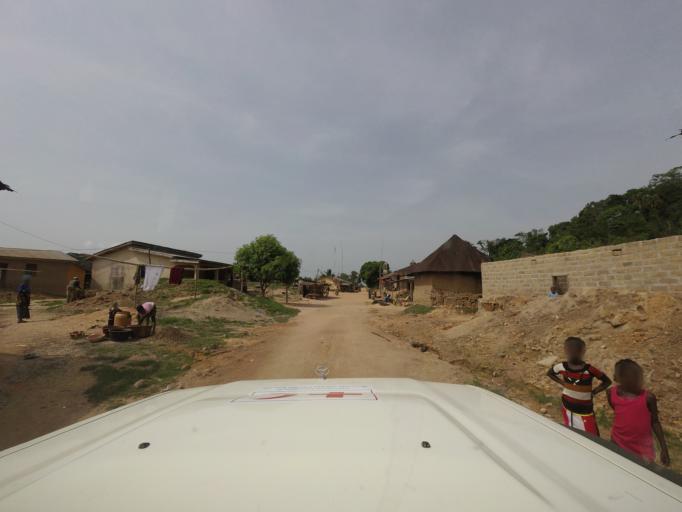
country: GN
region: Nzerekore
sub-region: Macenta
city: Macenta
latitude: 8.4563
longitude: -9.5868
